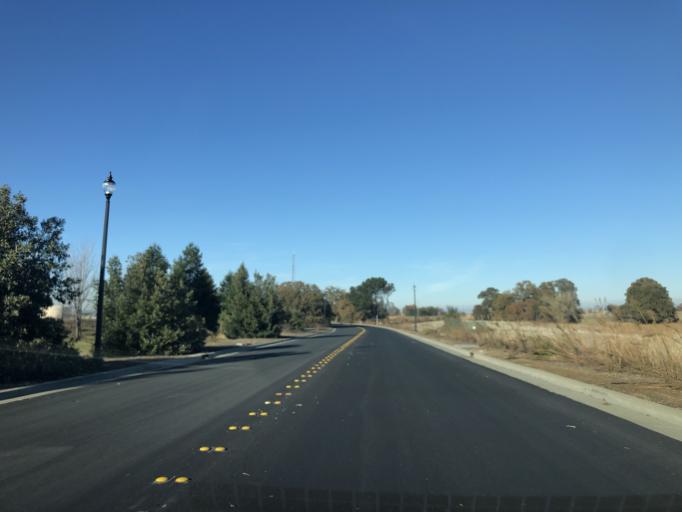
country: US
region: California
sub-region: Sacramento County
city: Antelope
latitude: 38.7880
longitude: -121.3772
